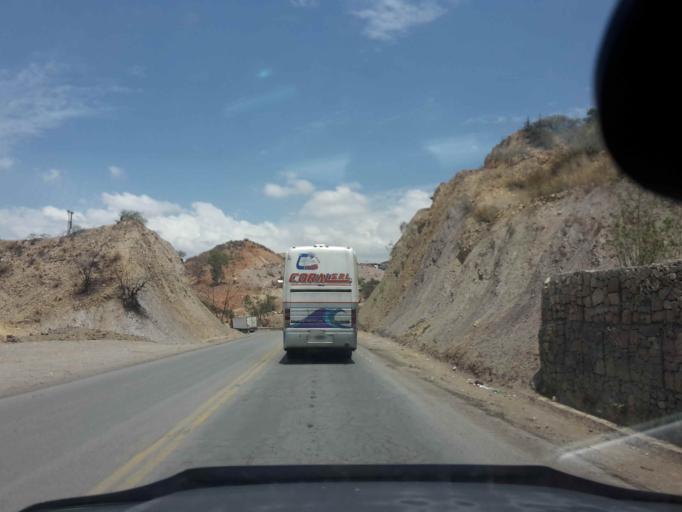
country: BO
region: Cochabamba
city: Sipe Sipe
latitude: -17.5512
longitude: -66.3418
